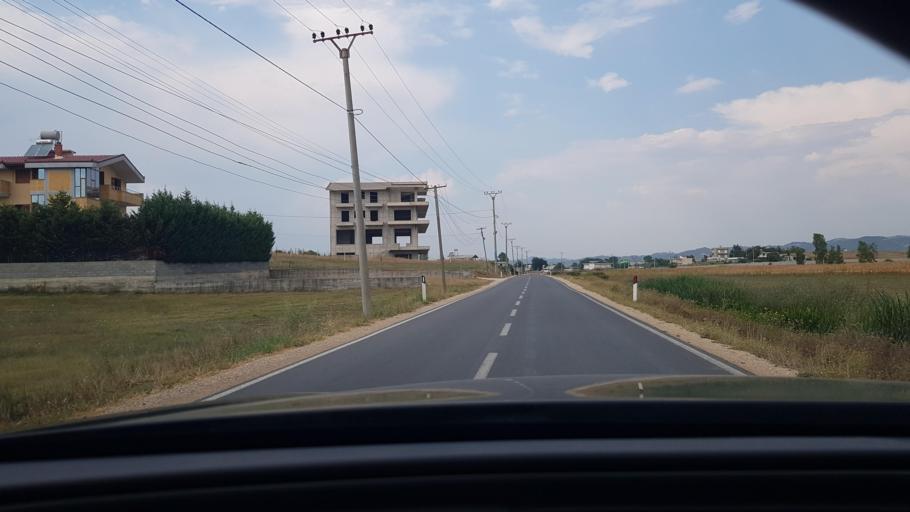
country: AL
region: Durres
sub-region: Rrethi i Durresit
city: Katundi i Ri
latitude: 41.4169
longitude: 19.5463
